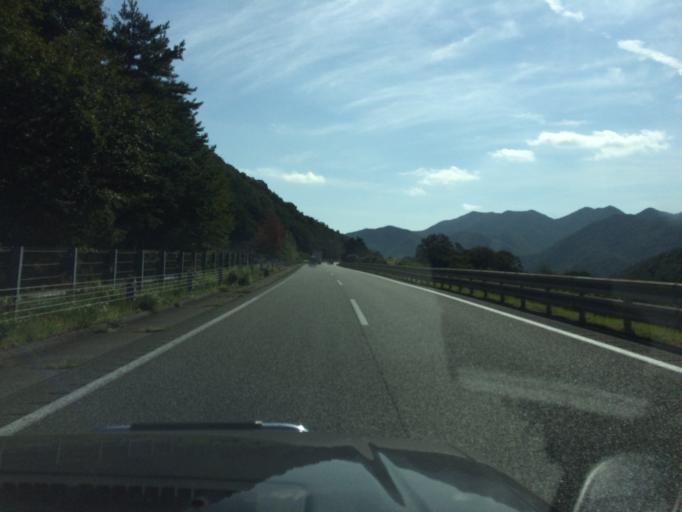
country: JP
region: Hyogo
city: Sasayama
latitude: 35.0126
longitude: 135.1625
